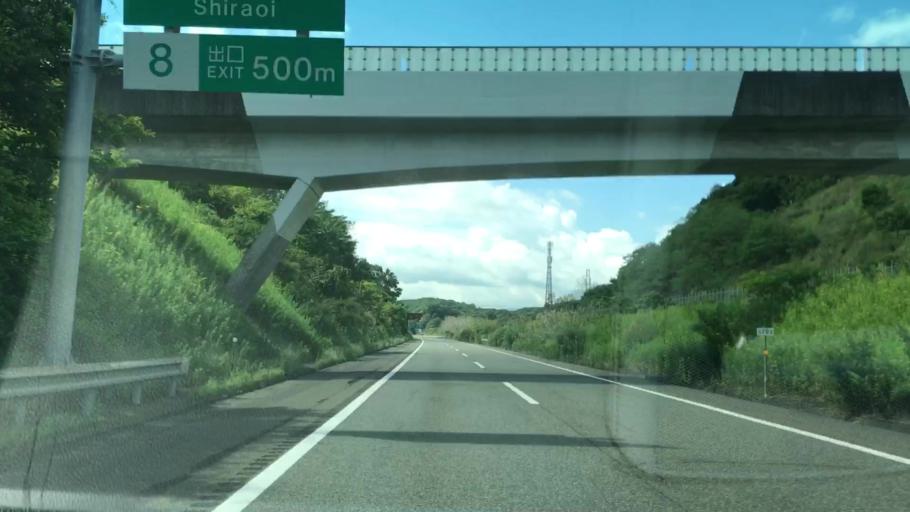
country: JP
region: Hokkaido
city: Shiraoi
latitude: 42.5682
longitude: 141.3372
